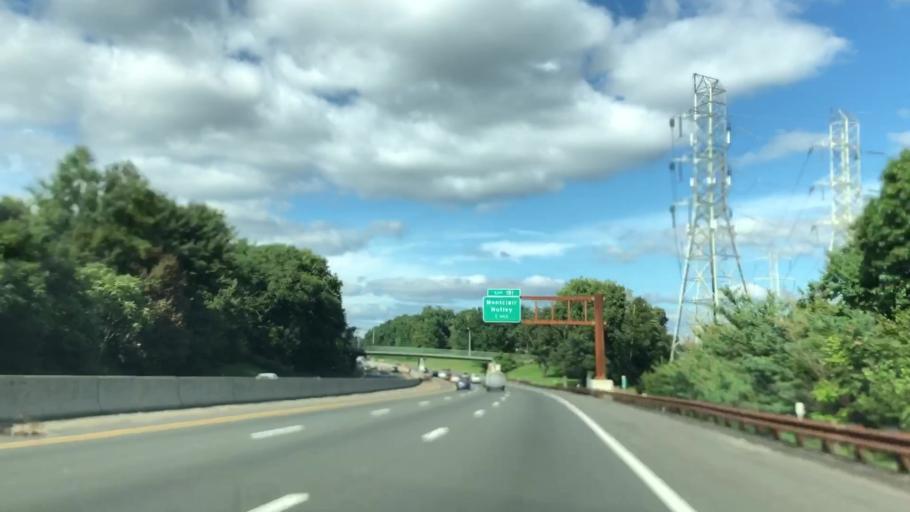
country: US
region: New Jersey
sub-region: Essex County
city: Bloomfield
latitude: 40.8113
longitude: -74.1801
